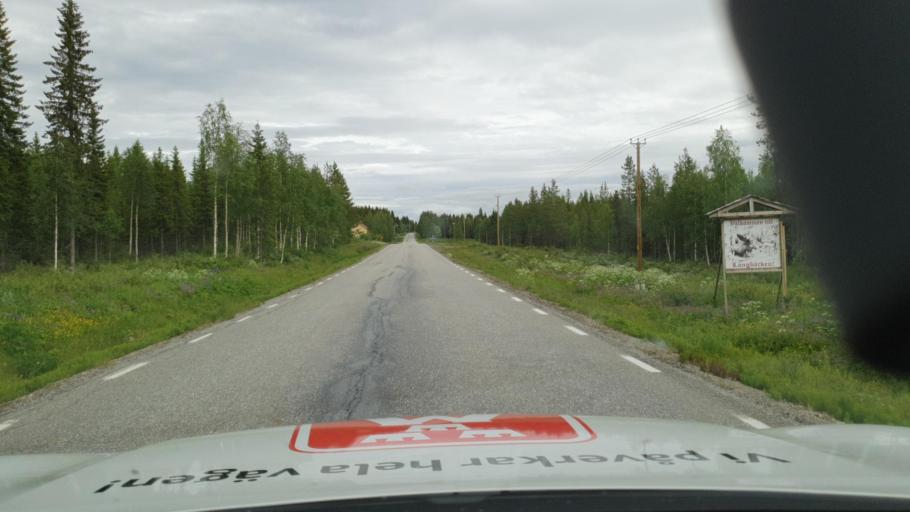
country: SE
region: Vaesterbotten
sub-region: Lycksele Kommun
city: Soderfors
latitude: 64.3653
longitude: 18.0880
